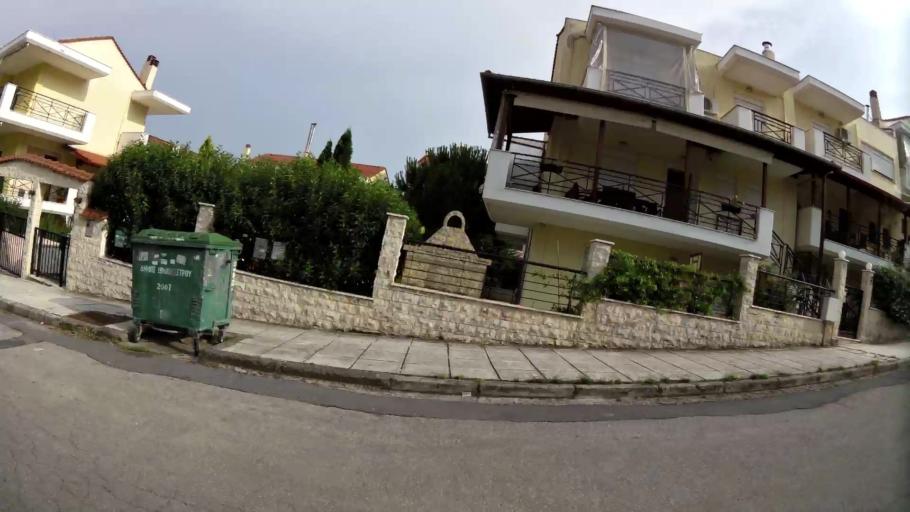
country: GR
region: Central Macedonia
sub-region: Nomos Thessalonikis
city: Oraiokastro
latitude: 40.7267
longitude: 22.9176
